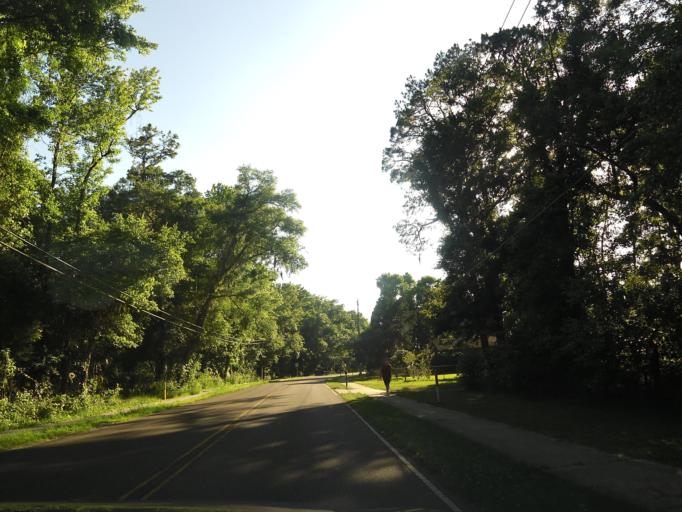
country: US
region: Florida
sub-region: Duval County
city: Jacksonville
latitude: 30.4634
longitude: -81.5599
